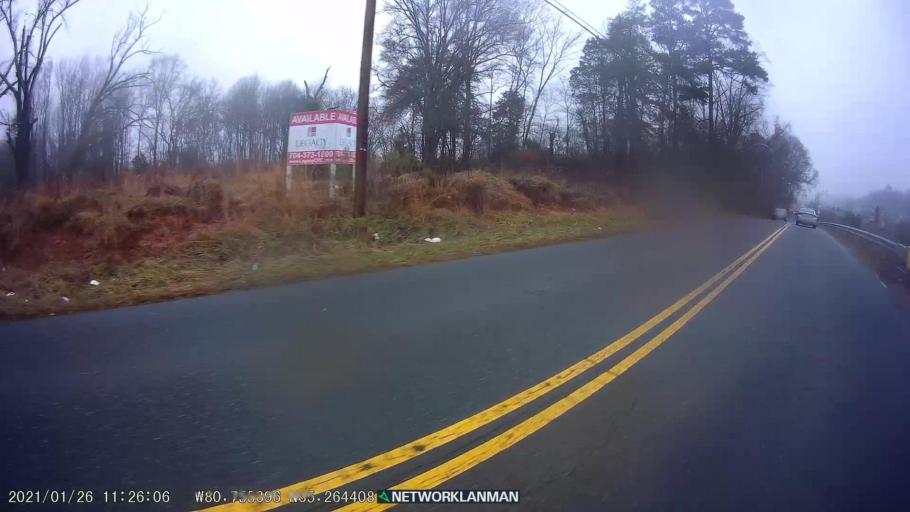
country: US
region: North Carolina
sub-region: Mecklenburg County
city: Charlotte
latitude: 35.2645
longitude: -80.7551
